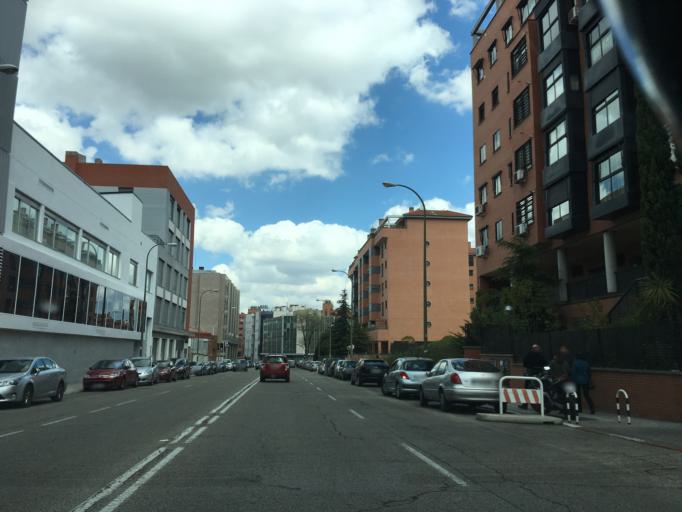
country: ES
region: Madrid
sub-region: Provincia de Madrid
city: San Blas
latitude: 40.4349
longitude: -3.6221
